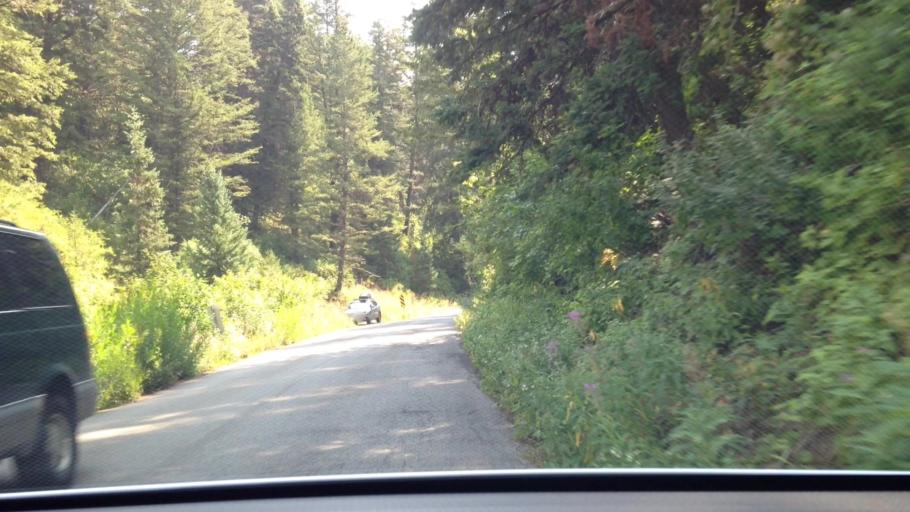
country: US
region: Utah
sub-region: Summit County
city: Summit Park
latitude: 40.6895
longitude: -111.6601
